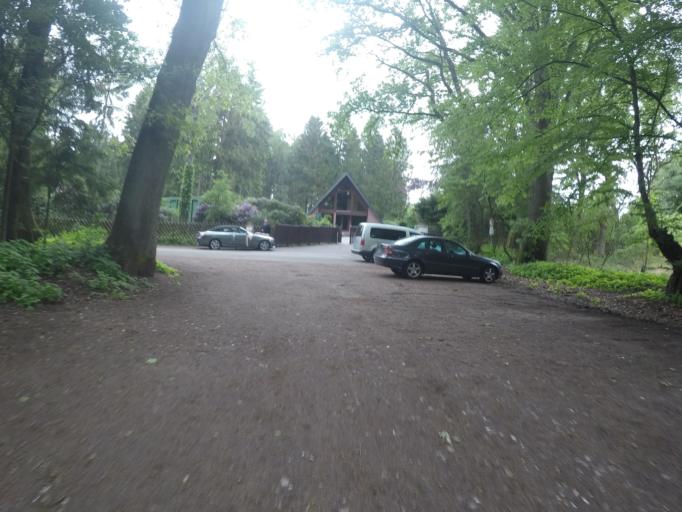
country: DE
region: Schleswig-Holstein
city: Bonningstedt
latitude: 53.6760
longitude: 9.9293
